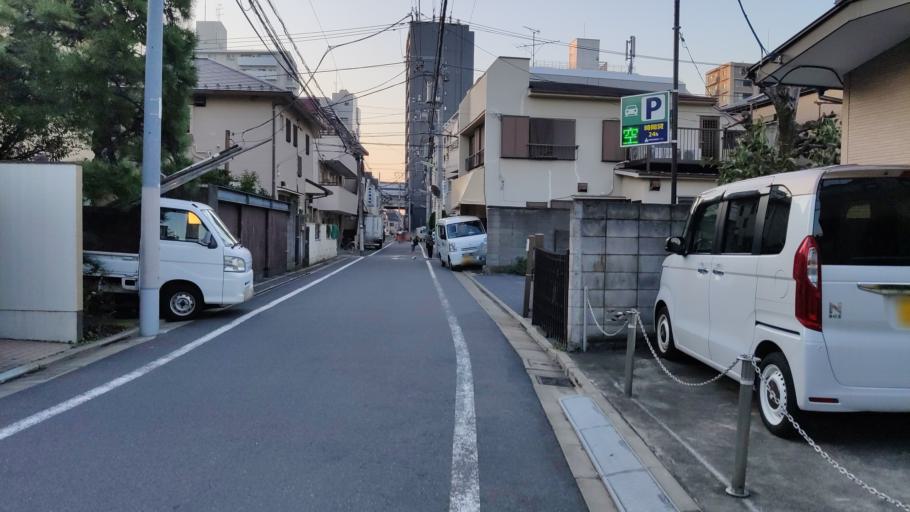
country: JP
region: Tokyo
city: Tokyo
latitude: 35.6355
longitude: 139.6672
